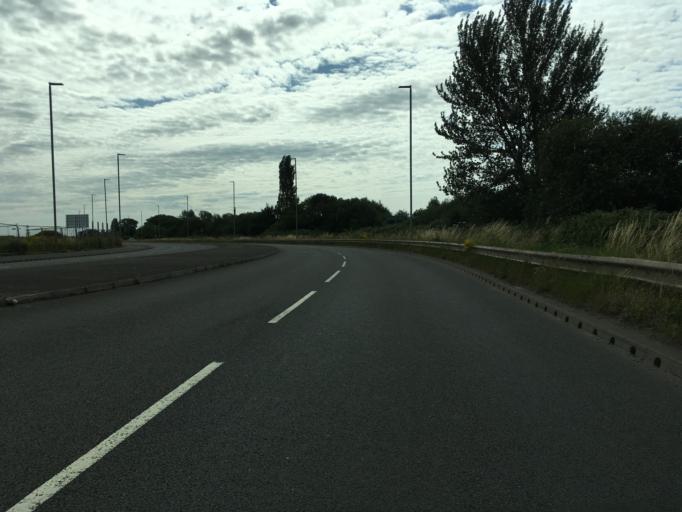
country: GB
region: Wales
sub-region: Newport
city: Llanwern
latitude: 51.5730
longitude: -2.9311
